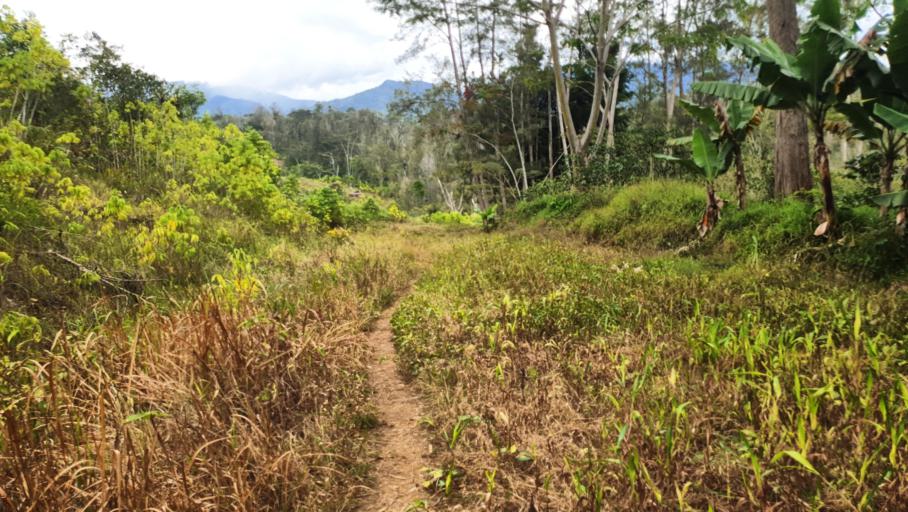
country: PG
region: Jiwaka
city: Minj
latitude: -5.9139
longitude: 144.8259
